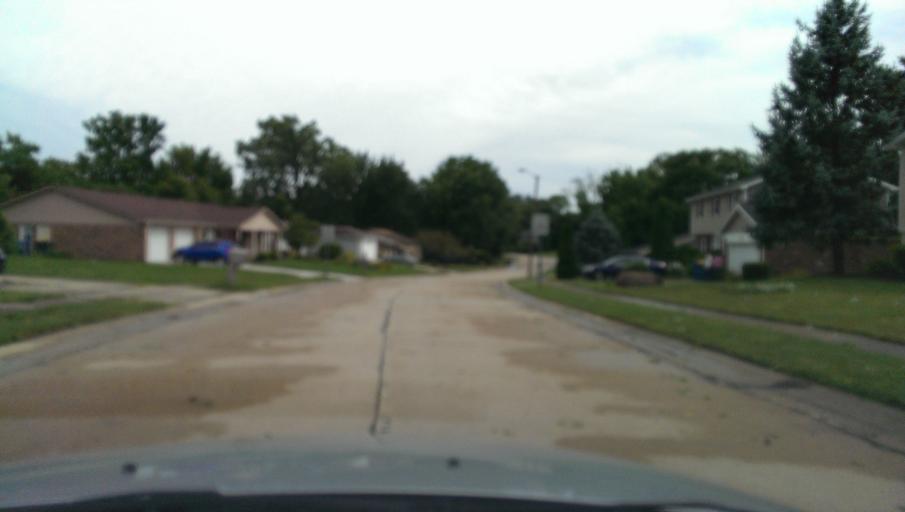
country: US
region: Indiana
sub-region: Hamilton County
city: Carmel
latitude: 39.9946
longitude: -86.1325
